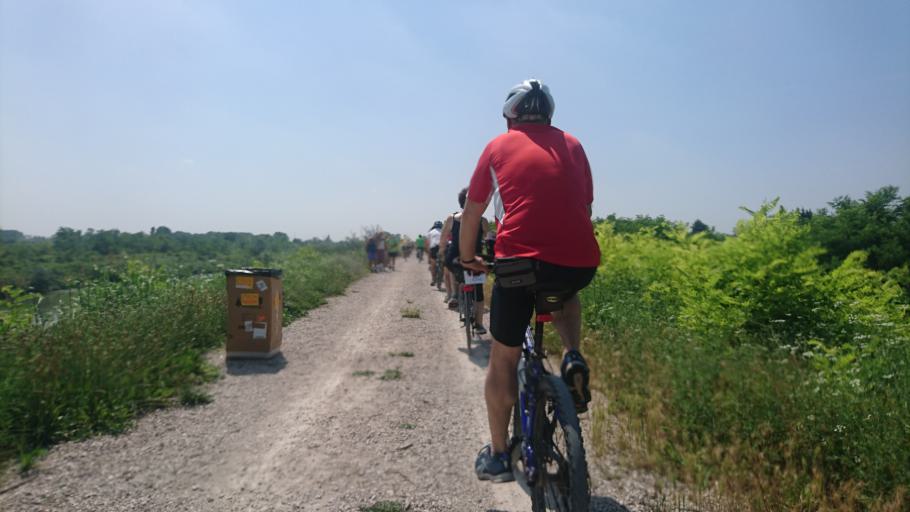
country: IT
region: Veneto
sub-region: Provincia di Padova
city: Oltre Brenta
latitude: 45.4011
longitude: 12.0028
